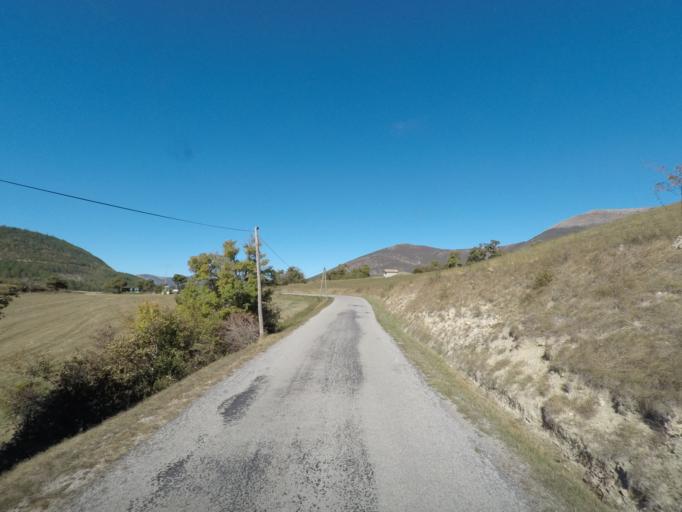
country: FR
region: Rhone-Alpes
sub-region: Departement de la Drome
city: Die
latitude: 44.5559
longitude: 5.3505
